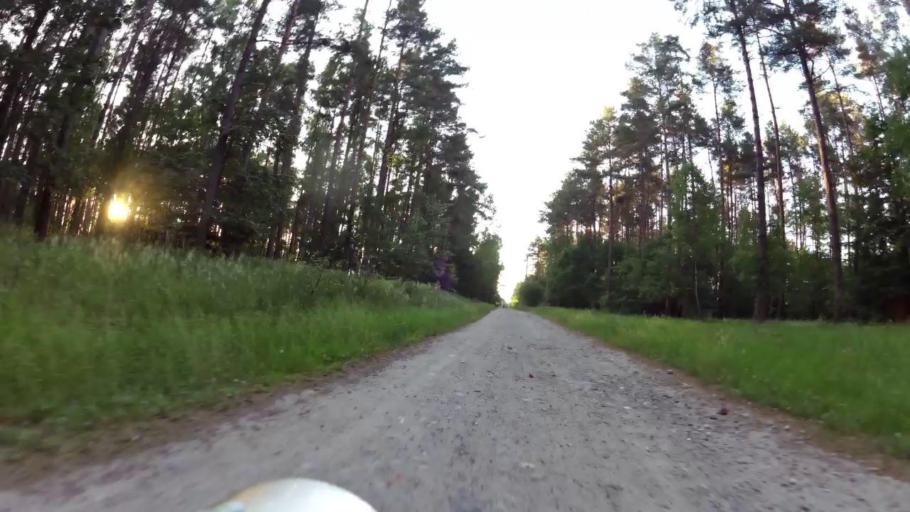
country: PL
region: West Pomeranian Voivodeship
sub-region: Powiat szczecinecki
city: Szczecinek
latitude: 53.8346
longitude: 16.6887
